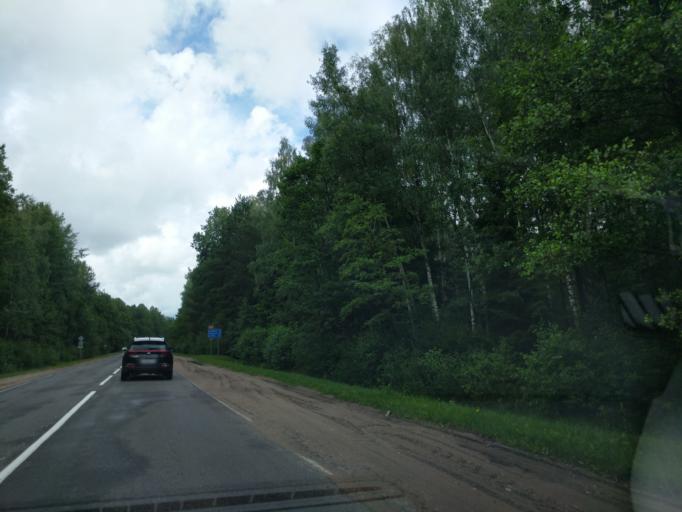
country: BY
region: Minsk
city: Il'ya
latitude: 54.4131
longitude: 27.2636
